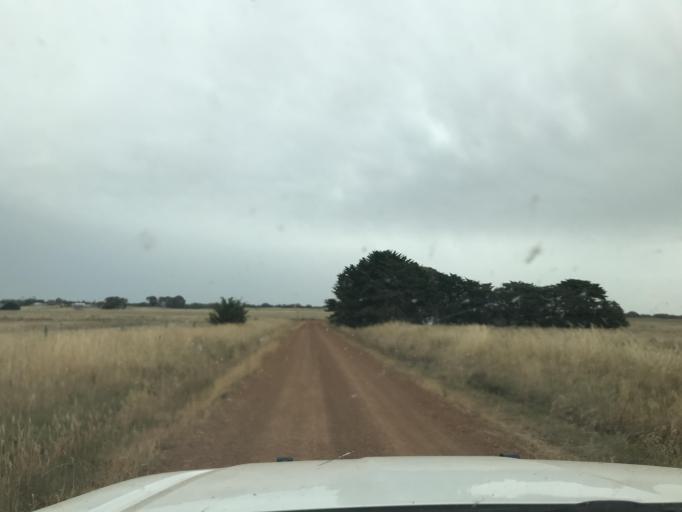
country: AU
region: Victoria
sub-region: Horsham
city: Horsham
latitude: -37.0595
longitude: 141.6011
